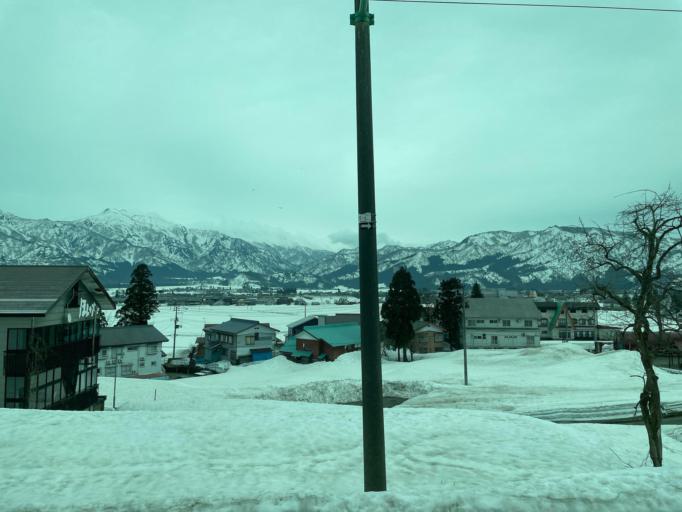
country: JP
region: Niigata
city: Shiozawa
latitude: 37.0304
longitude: 138.8318
